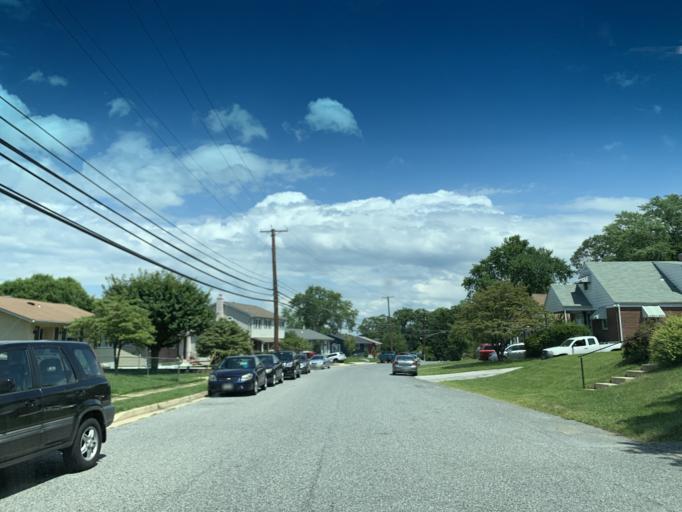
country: US
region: Maryland
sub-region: Baltimore County
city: Timonium
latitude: 39.4402
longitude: -76.6198
